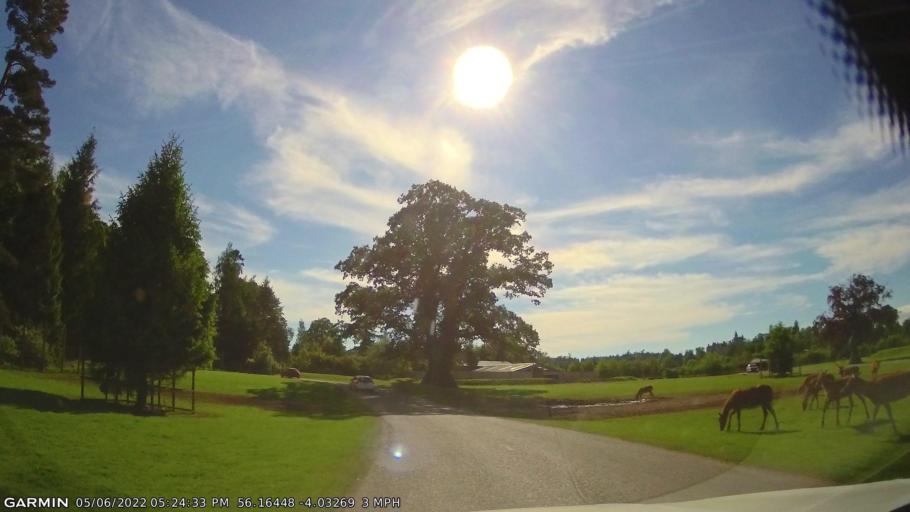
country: GB
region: Scotland
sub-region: Stirling
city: Doune
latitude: 56.1645
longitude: -4.0325
